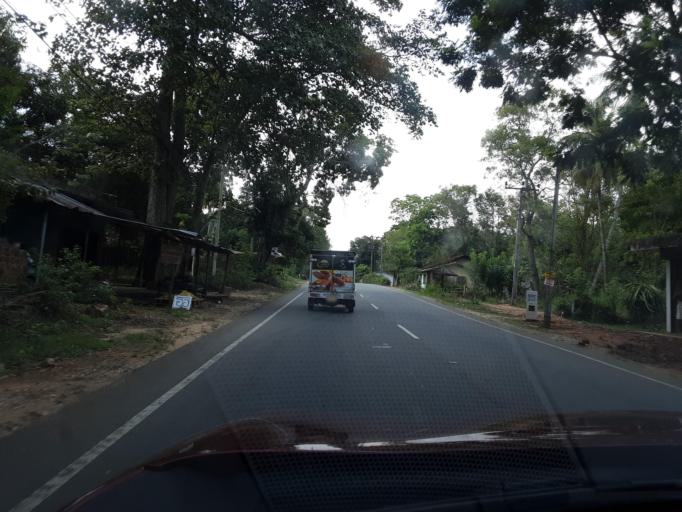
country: LK
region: Uva
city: Haputale
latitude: 6.6848
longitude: 81.1086
